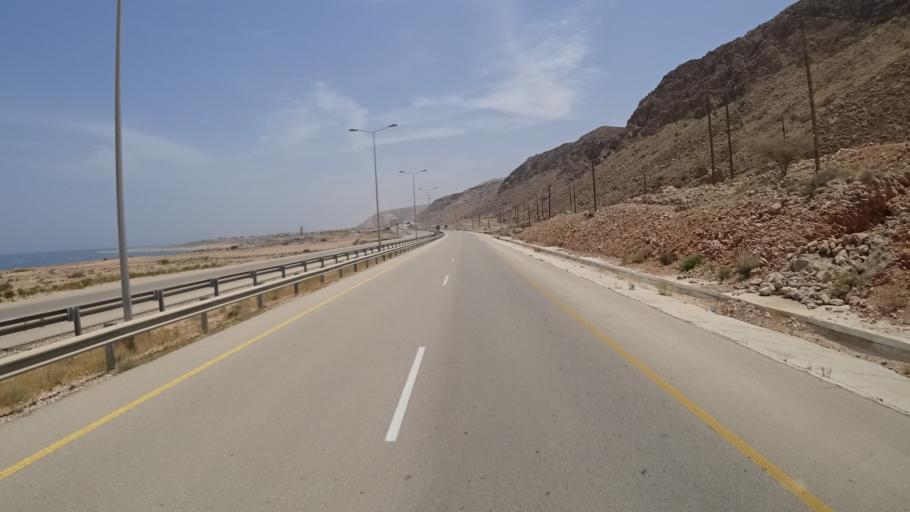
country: OM
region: Ash Sharqiyah
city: Sur
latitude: 22.7141
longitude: 59.3526
